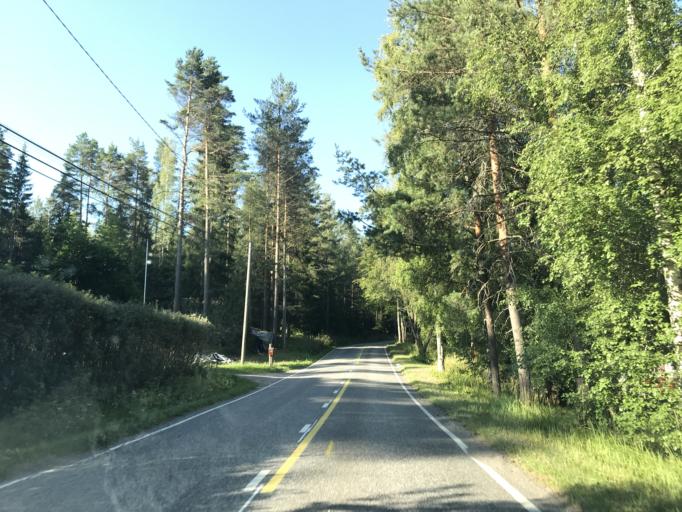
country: FI
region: Uusimaa
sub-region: Helsinki
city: Lohja
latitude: 60.2827
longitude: 24.1380
